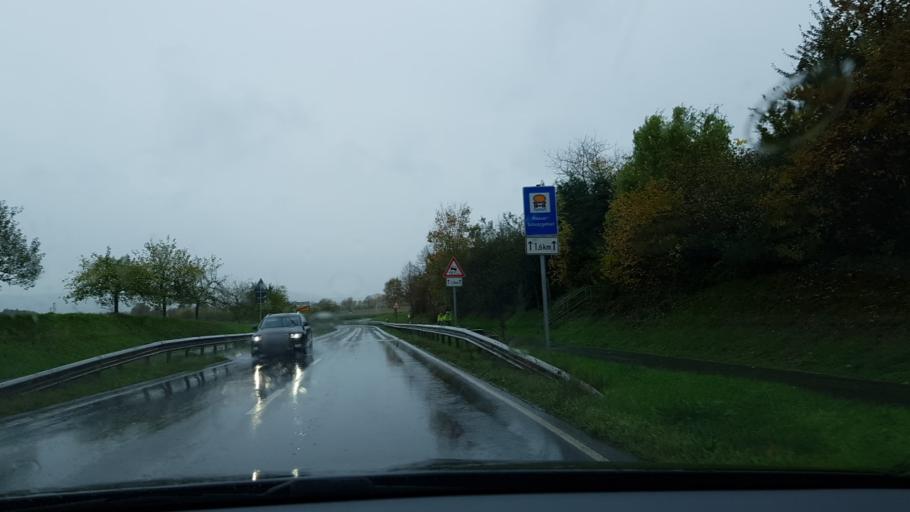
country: DE
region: Rheinland-Pfalz
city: Neuerburg
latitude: 49.9874
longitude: 6.9390
